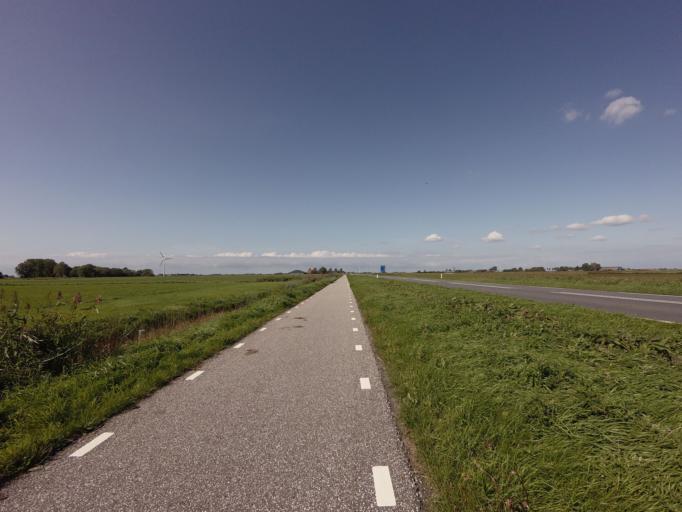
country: NL
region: Friesland
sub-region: Gemeente Littenseradiel
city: Makkum
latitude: 53.1125
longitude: 5.6843
